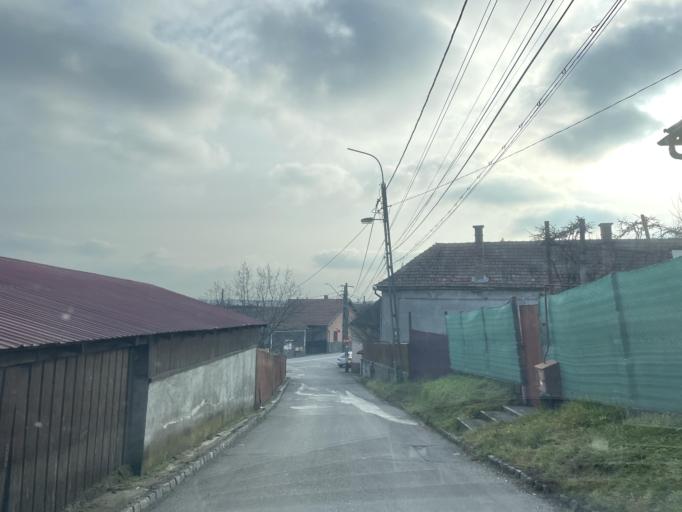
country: RO
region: Mures
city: Reghin-Sat
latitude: 46.7887
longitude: 24.7106
